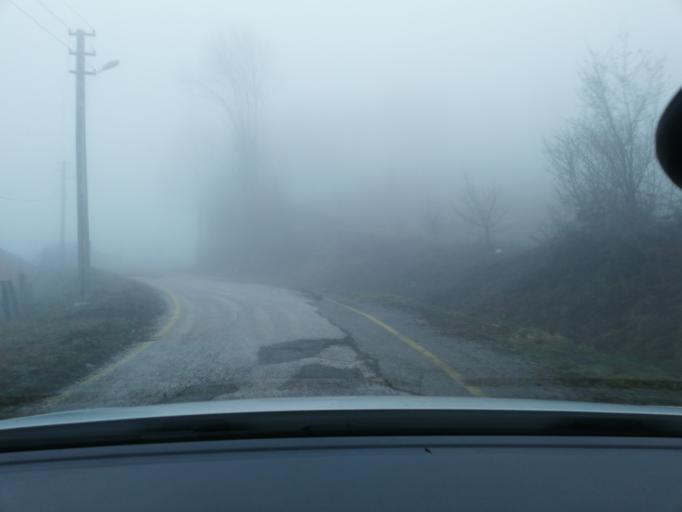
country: TR
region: Duzce
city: Kaynasli
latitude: 40.7525
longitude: 31.3768
